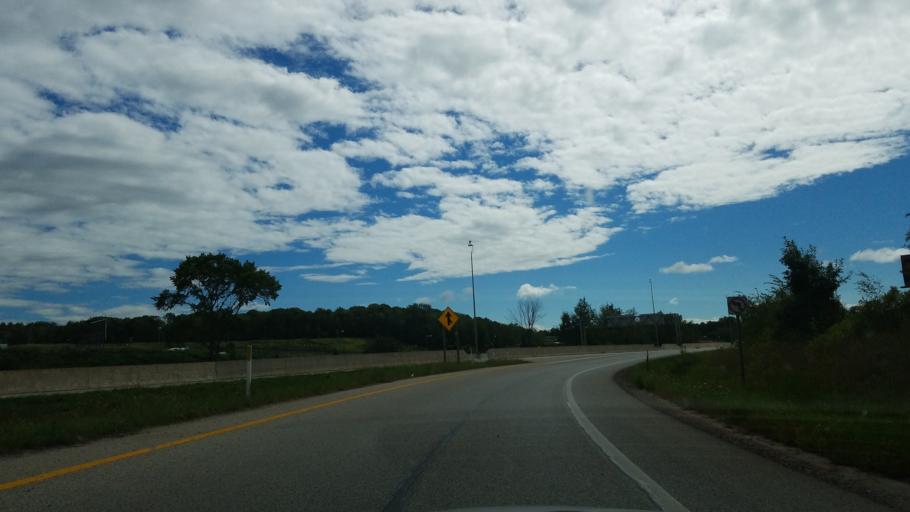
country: US
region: Michigan
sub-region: Chippewa County
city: Sault Ste. Marie
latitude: 46.4905
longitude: -84.3733
